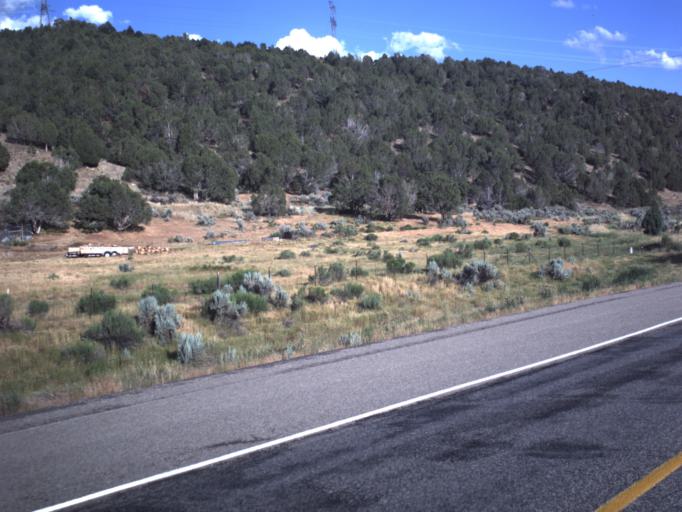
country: US
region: Utah
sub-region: Utah County
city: Woodland Hills
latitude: 39.8898
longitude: -111.5483
